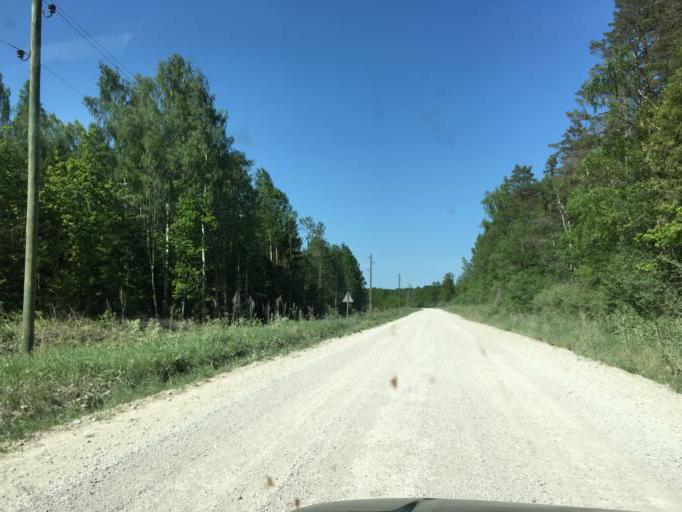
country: LV
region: Dundaga
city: Dundaga
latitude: 57.4458
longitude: 22.3207
